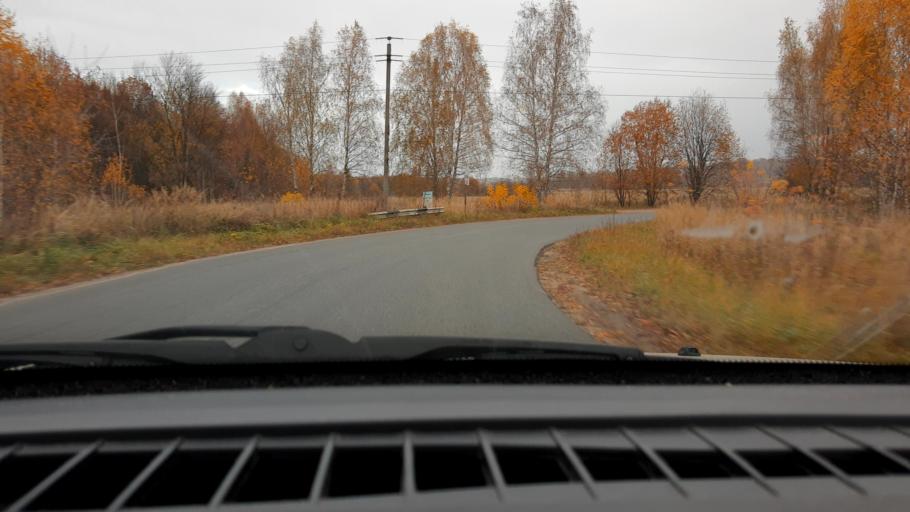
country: RU
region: Nizjnij Novgorod
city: Burevestnik
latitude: 56.0544
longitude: 43.8517
